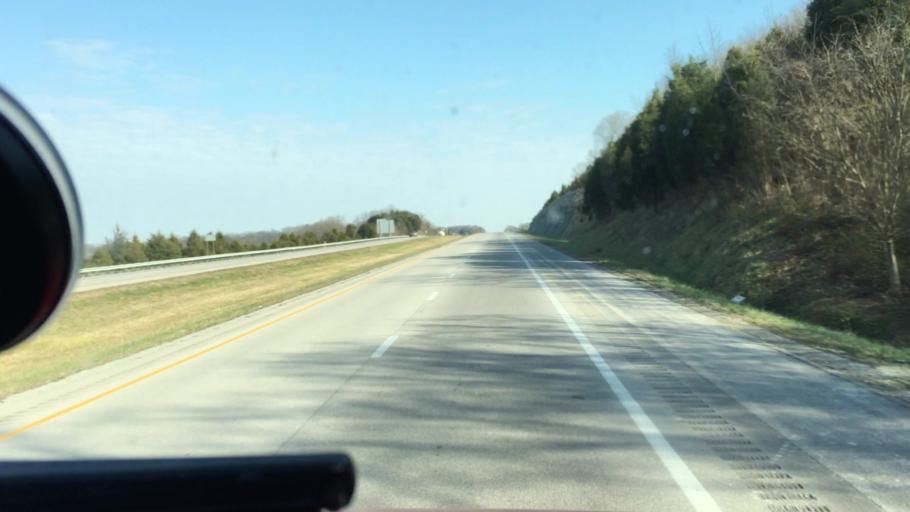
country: US
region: Kentucky
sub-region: Bath County
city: Owingsville
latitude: 38.1340
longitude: -83.7351
